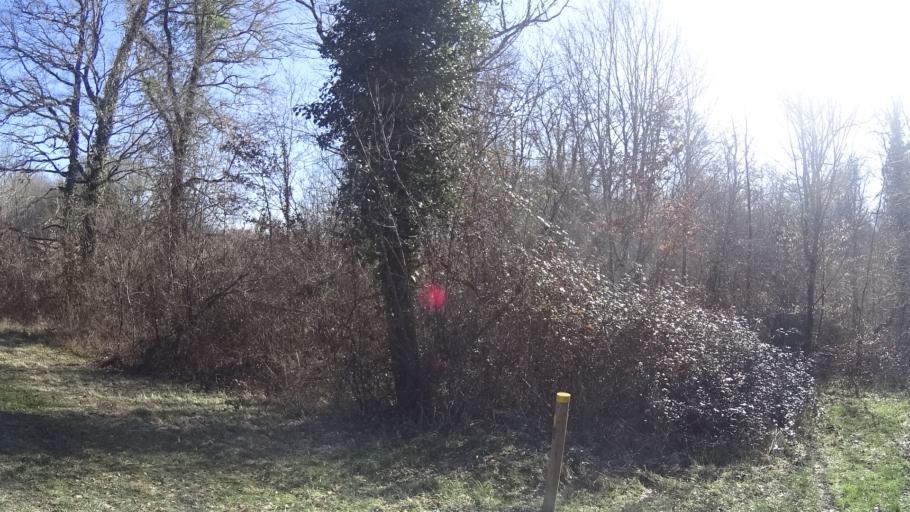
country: FR
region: Aquitaine
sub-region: Departement de la Dordogne
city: Saint-Aulaye
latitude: 45.1186
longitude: 0.2048
